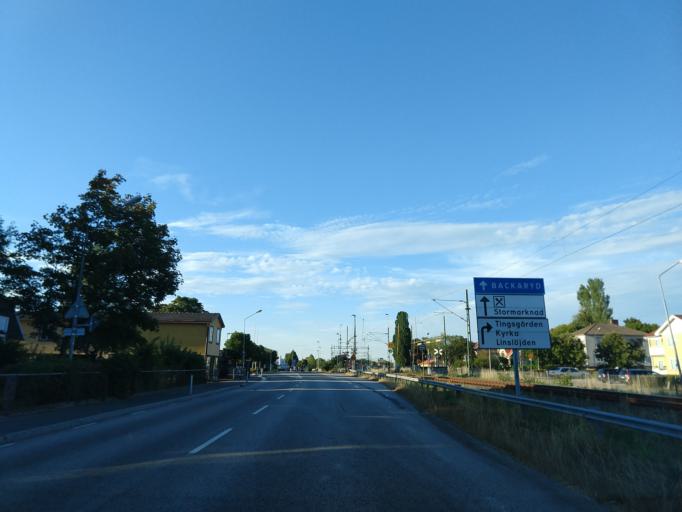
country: SE
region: Blekinge
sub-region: Ronneby Kommun
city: Brakne-Hoby
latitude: 56.2289
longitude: 15.1148
